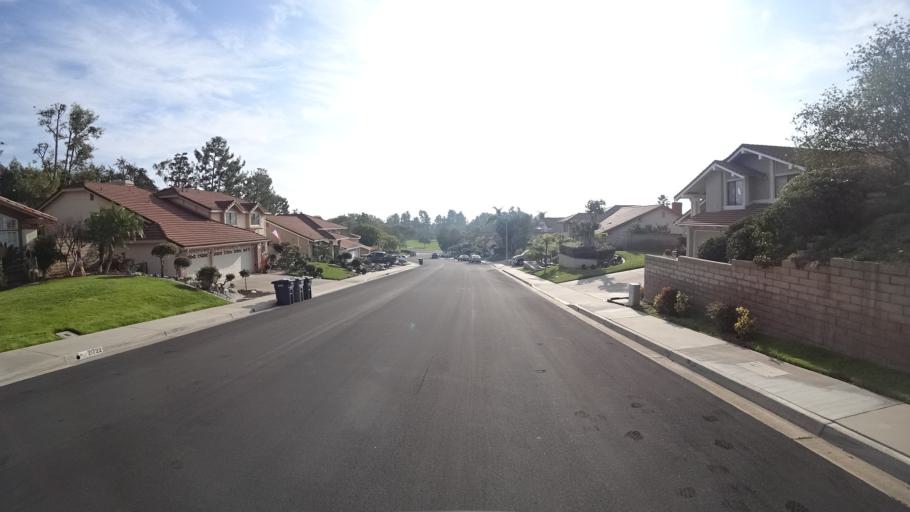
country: US
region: California
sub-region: Orange County
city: Lake Forest
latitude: 33.6472
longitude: -117.6788
